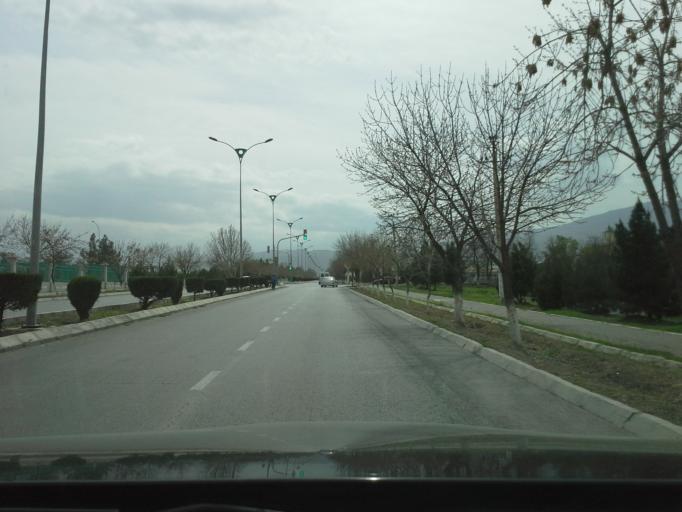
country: TM
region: Ahal
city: Abadan
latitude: 38.0611
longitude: 58.1590
